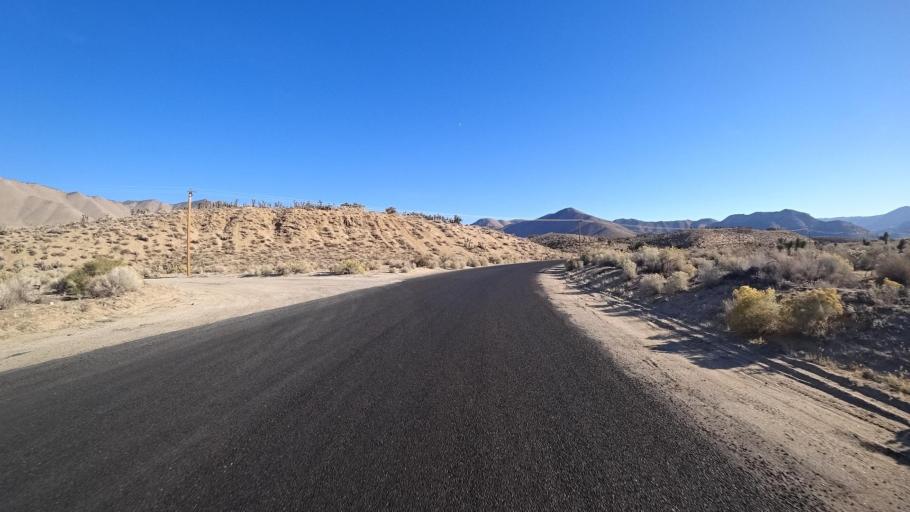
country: US
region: California
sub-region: Kern County
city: Weldon
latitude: 35.6117
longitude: -118.2438
